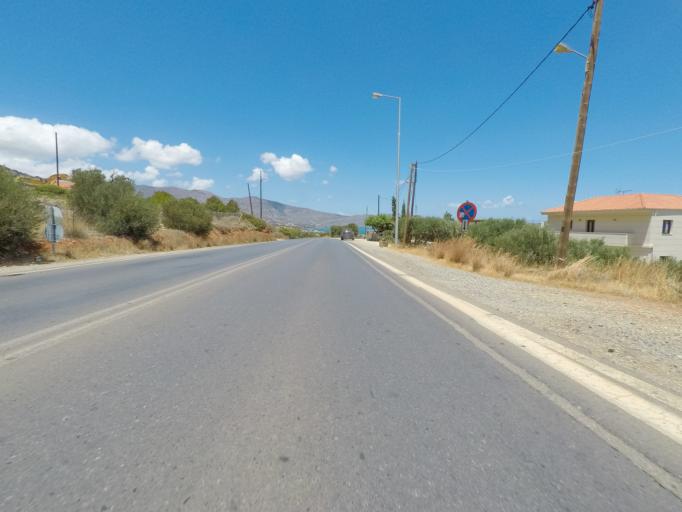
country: GR
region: Crete
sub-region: Nomos Lasithiou
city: Skhisma
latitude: 35.2436
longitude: 25.7258
